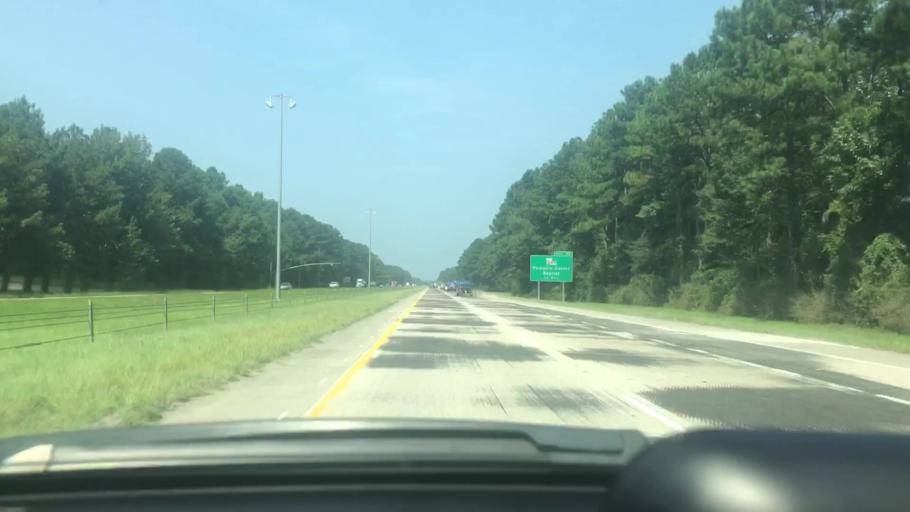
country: US
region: Louisiana
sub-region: Livingston Parish
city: Albany
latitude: 30.4795
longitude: -90.5280
